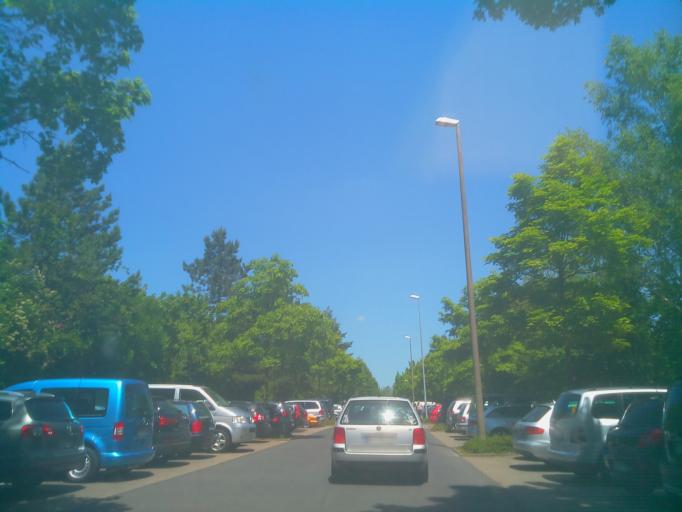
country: DE
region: Bavaria
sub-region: Regierungsbezirk Unterfranken
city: Sennfeld
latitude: 50.0654
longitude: 10.2474
